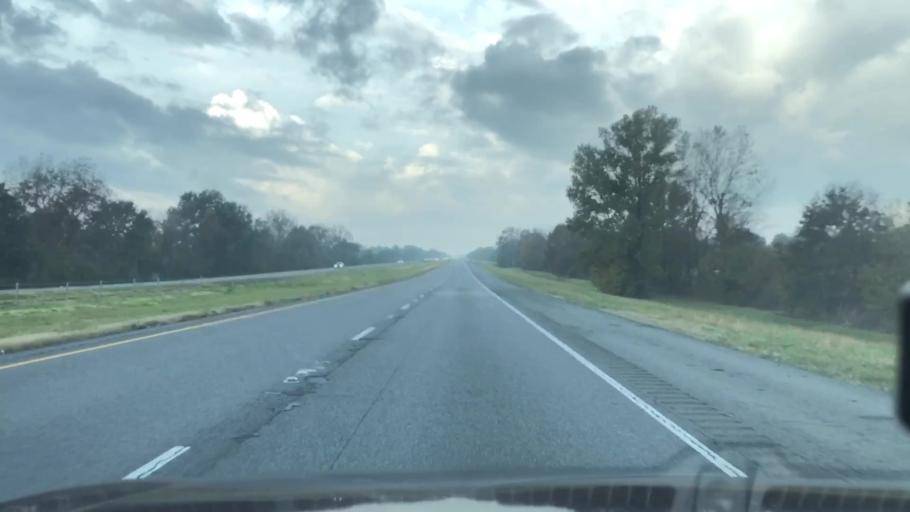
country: US
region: Louisiana
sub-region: Madison Parish
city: Tallulah
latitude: 32.4057
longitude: -91.2292
